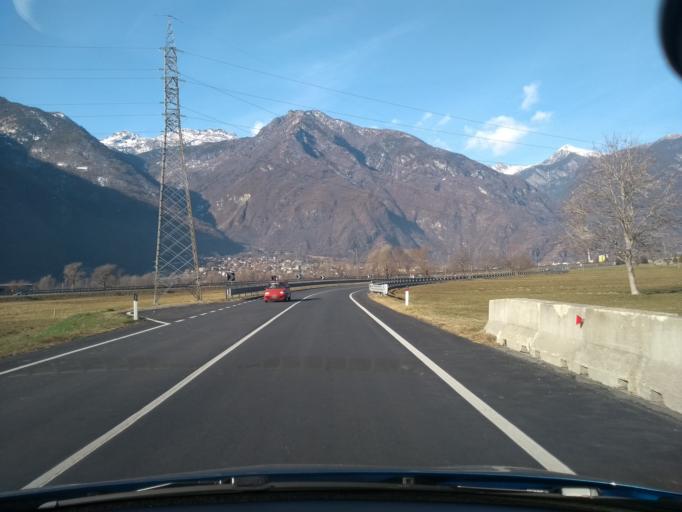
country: IT
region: Aosta Valley
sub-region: Valle d'Aosta
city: Arnad
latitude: 45.6530
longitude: 7.7043
